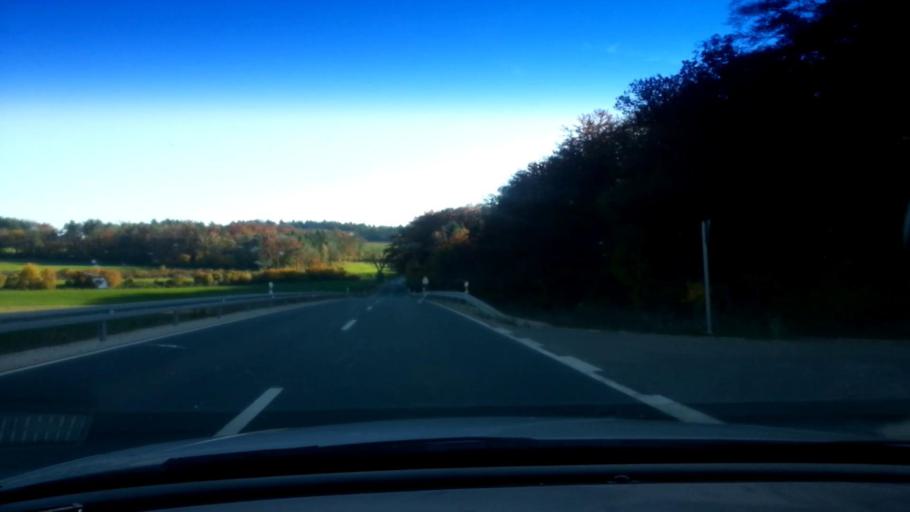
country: DE
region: Bavaria
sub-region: Upper Franconia
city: Poxdorf
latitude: 49.9213
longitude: 11.0889
